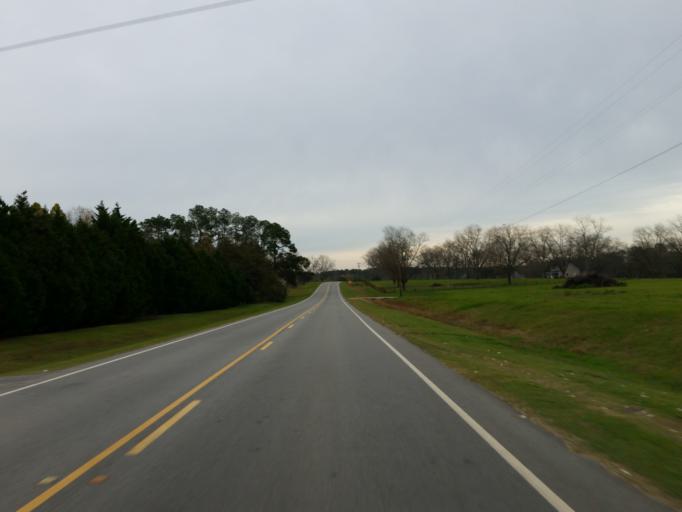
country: US
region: Georgia
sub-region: Turner County
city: Ashburn
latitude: 31.6667
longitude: -83.6231
